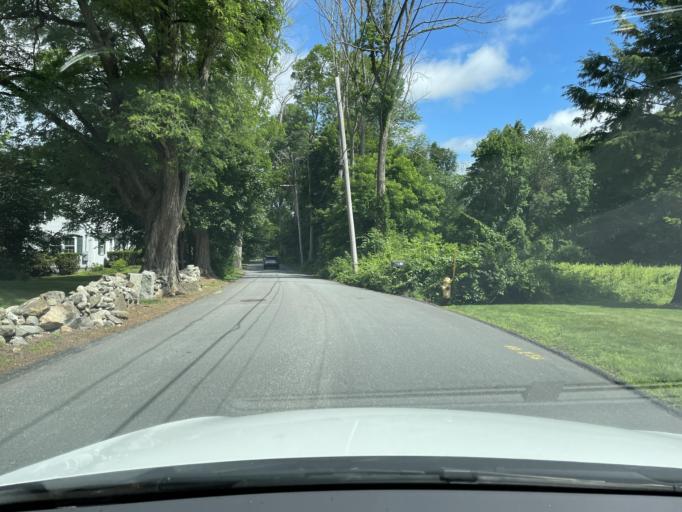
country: US
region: Massachusetts
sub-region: Essex County
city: Andover
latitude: 42.6454
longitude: -71.1241
